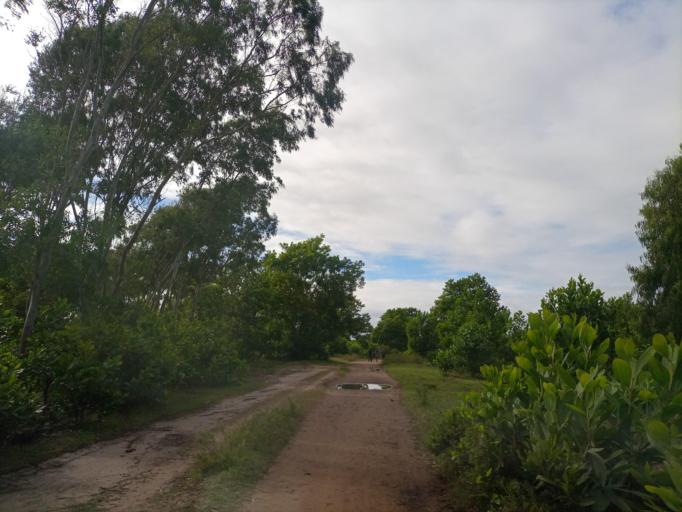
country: MG
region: Anosy
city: Fort Dauphin
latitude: -24.7792
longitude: 47.1833
